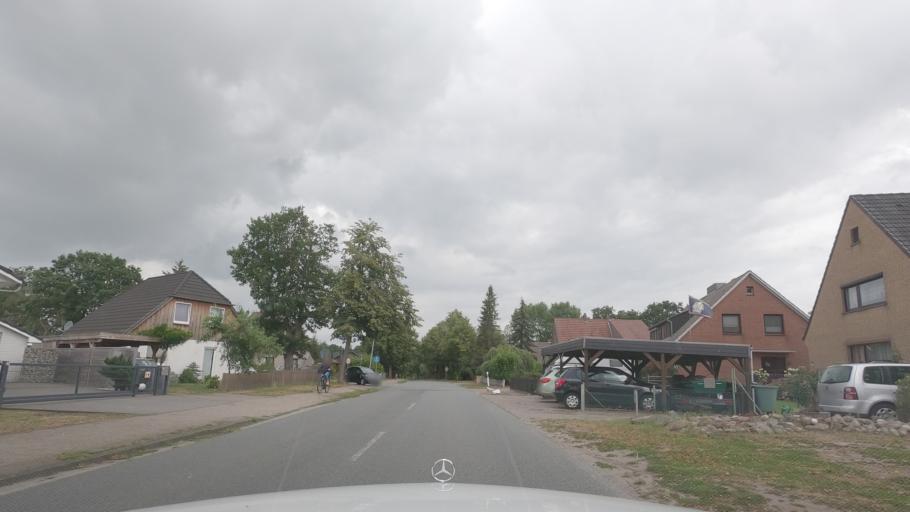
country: DE
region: Lower Saxony
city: Neuenkirchen
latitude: 53.2298
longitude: 8.5296
